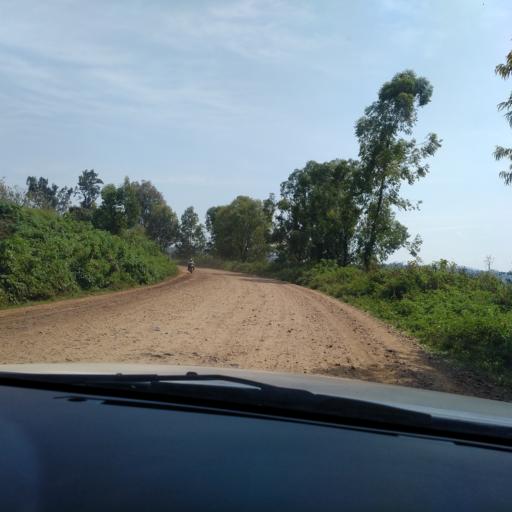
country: CD
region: South Kivu
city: Bukavu
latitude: -2.2095
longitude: 28.8357
